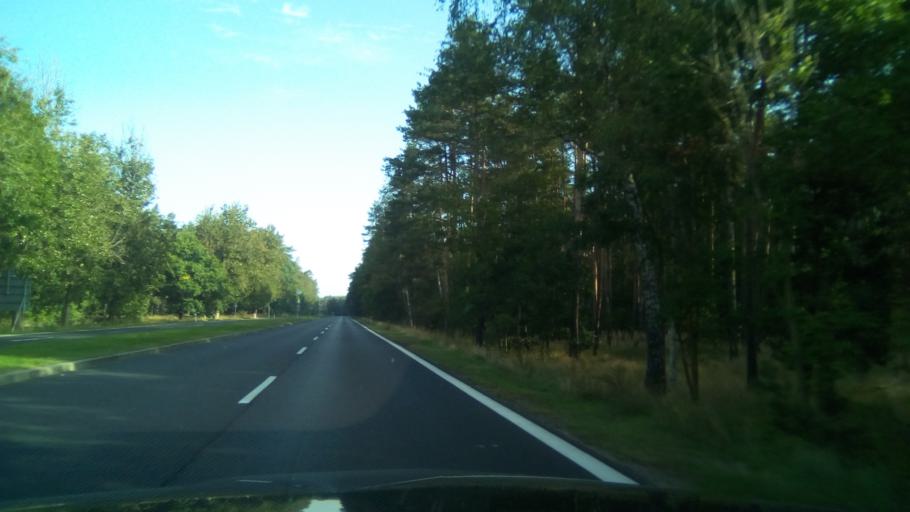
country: PL
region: Greater Poland Voivodeship
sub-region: Powiat pilski
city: Pila
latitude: 53.1148
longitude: 16.7512
